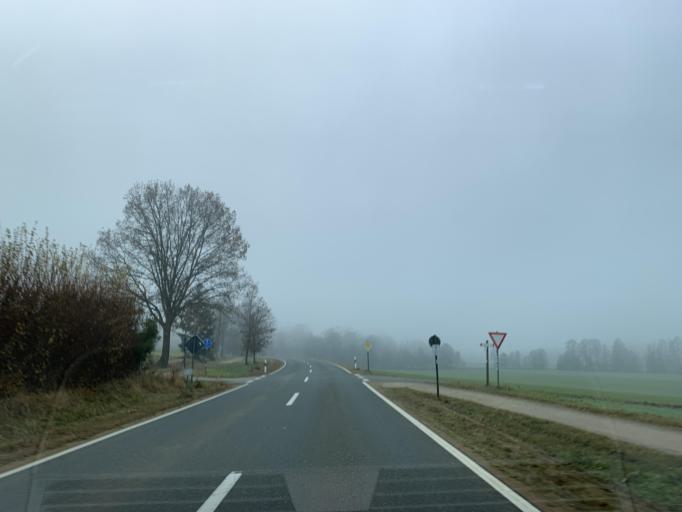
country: DE
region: Bavaria
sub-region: Upper Palatinate
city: Neunburg vorm Wald
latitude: 49.3599
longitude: 12.3979
